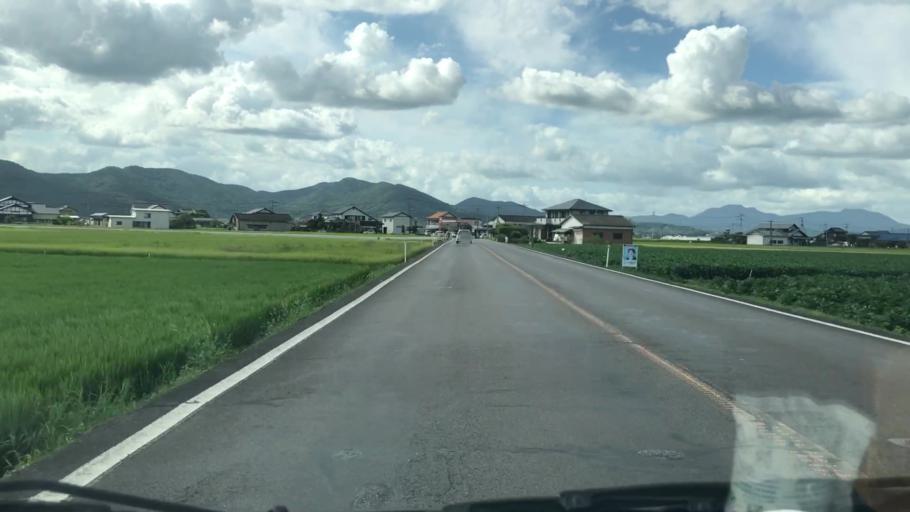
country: JP
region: Saga Prefecture
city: Kashima
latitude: 33.1381
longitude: 130.1380
